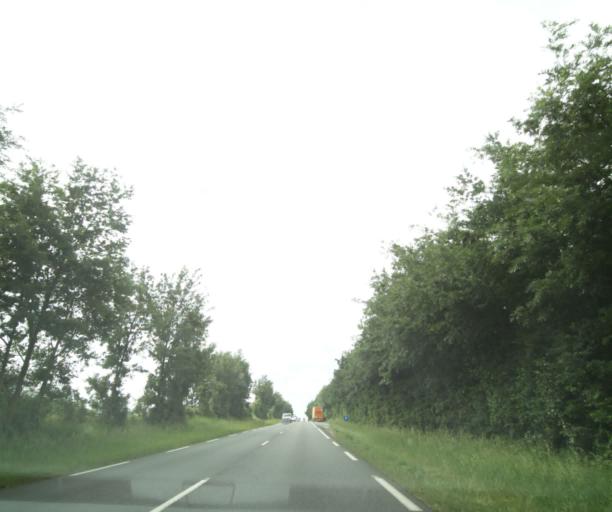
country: FR
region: Pays de la Loire
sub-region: Departement de Maine-et-Loire
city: Montreuil-Bellay
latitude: 47.1610
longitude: -0.1437
